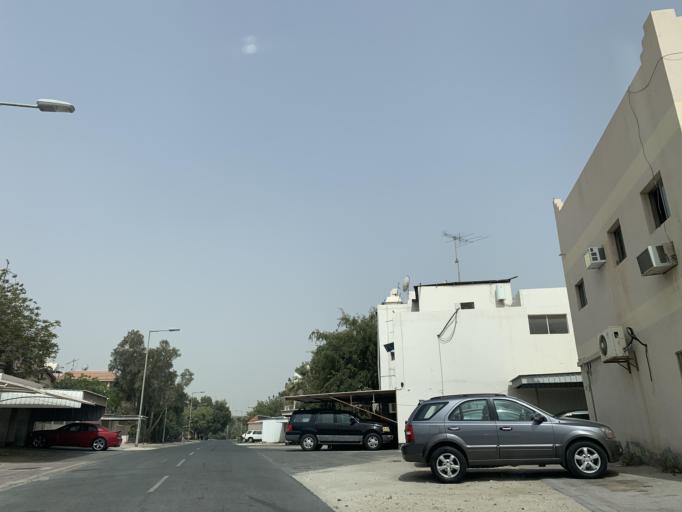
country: BH
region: Northern
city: Madinat `Isa
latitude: 26.1685
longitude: 50.5463
